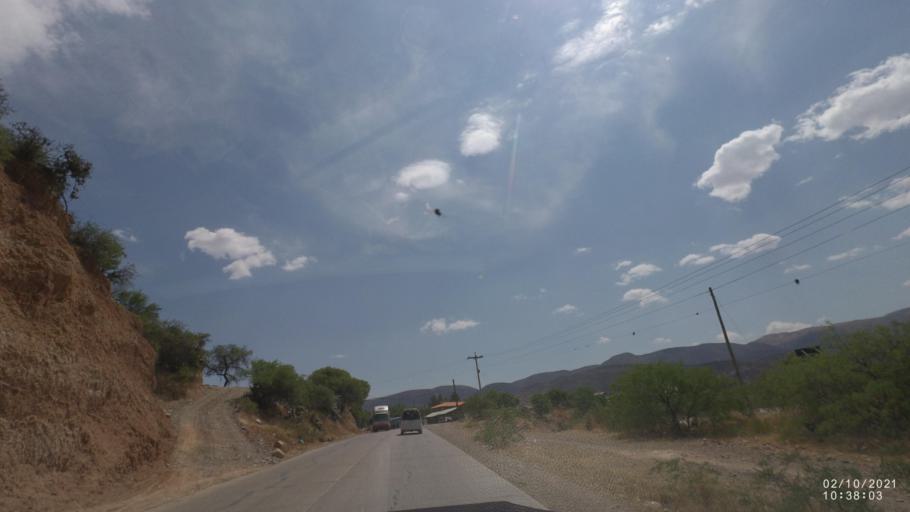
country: BO
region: Cochabamba
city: Capinota
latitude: -17.6365
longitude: -66.2655
